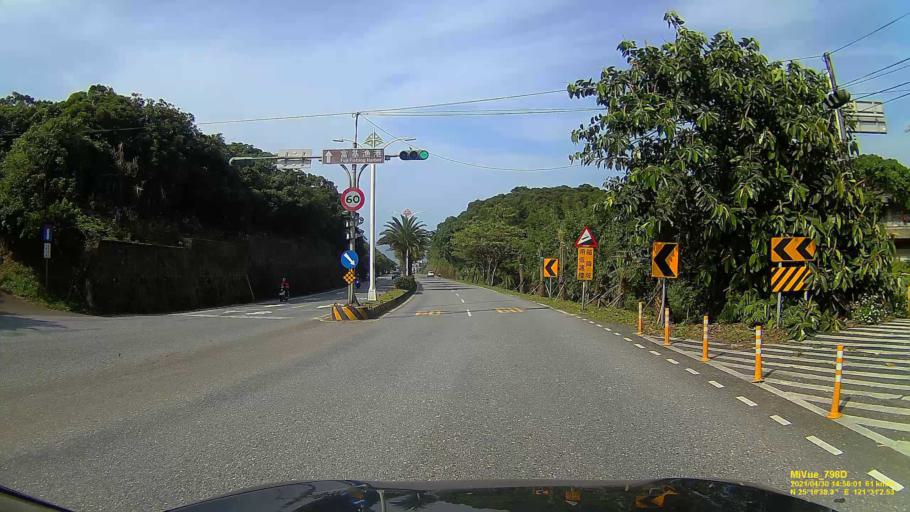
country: TW
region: Taipei
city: Taipei
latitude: 25.2777
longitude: 121.5177
